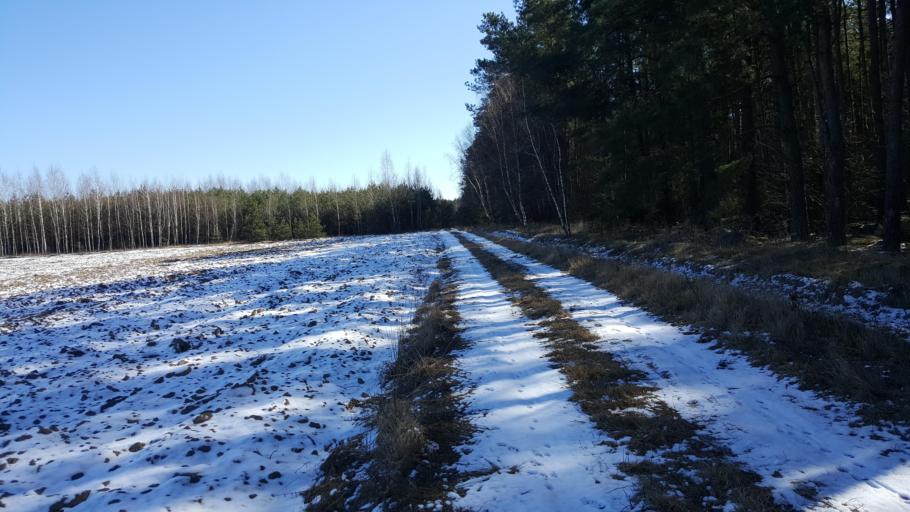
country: BY
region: Brest
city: Kamyanyets
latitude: 52.3705
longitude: 23.8124
